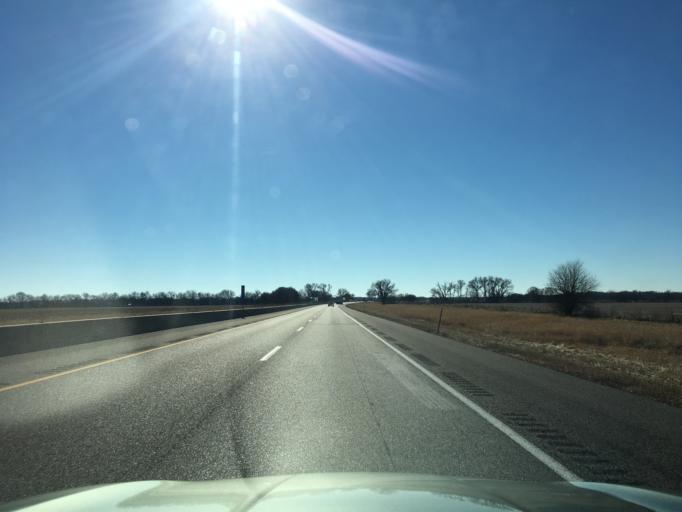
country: US
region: Kansas
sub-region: Sumner County
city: Belle Plaine
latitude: 37.4200
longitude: -97.3213
